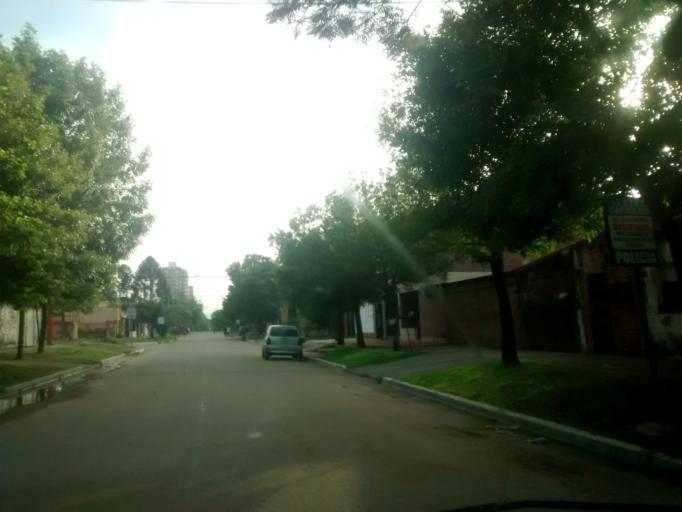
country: AR
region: Chaco
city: Resistencia
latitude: -27.4628
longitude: -58.9978
